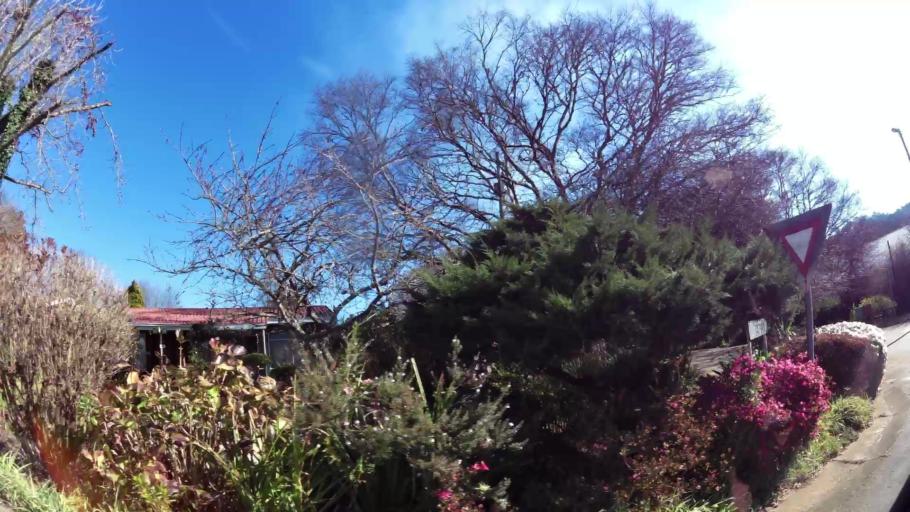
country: ZA
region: Limpopo
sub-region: Capricorn District Municipality
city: Mankoeng
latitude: -23.9427
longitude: 29.9397
